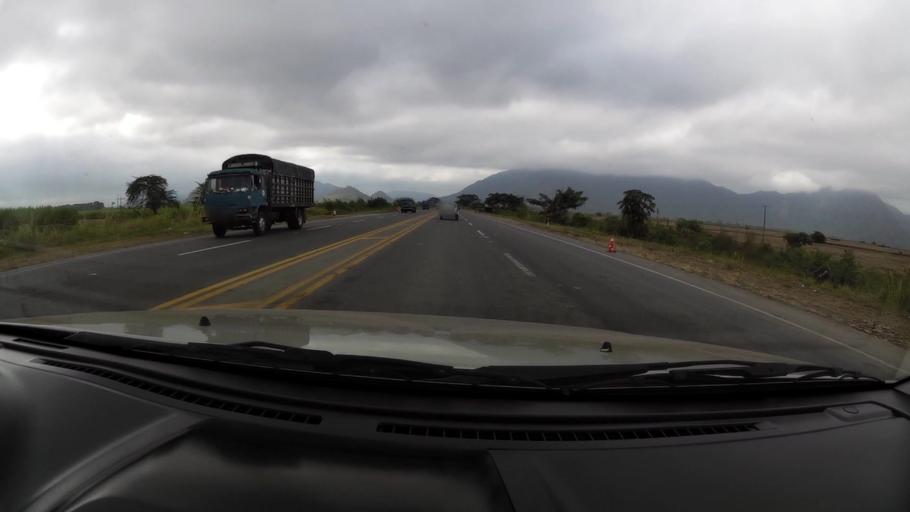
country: EC
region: Guayas
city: Coronel Marcelino Mariduena
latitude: -2.3579
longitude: -79.6335
